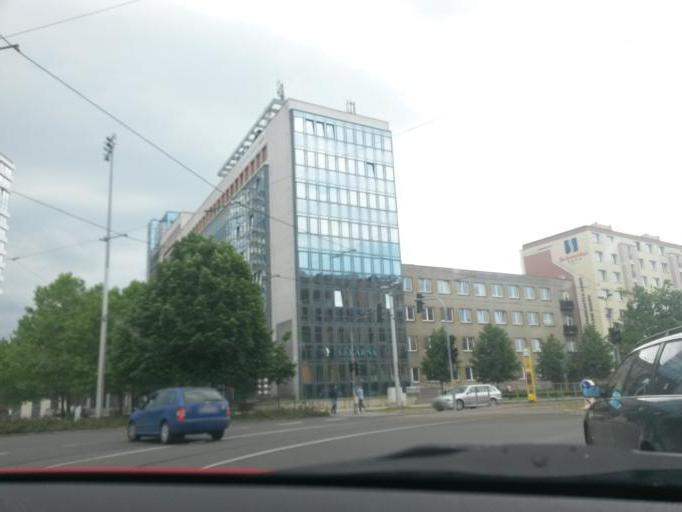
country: CZ
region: Olomoucky
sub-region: Okres Olomouc
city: Olomouc
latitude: 49.5923
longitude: 17.2764
